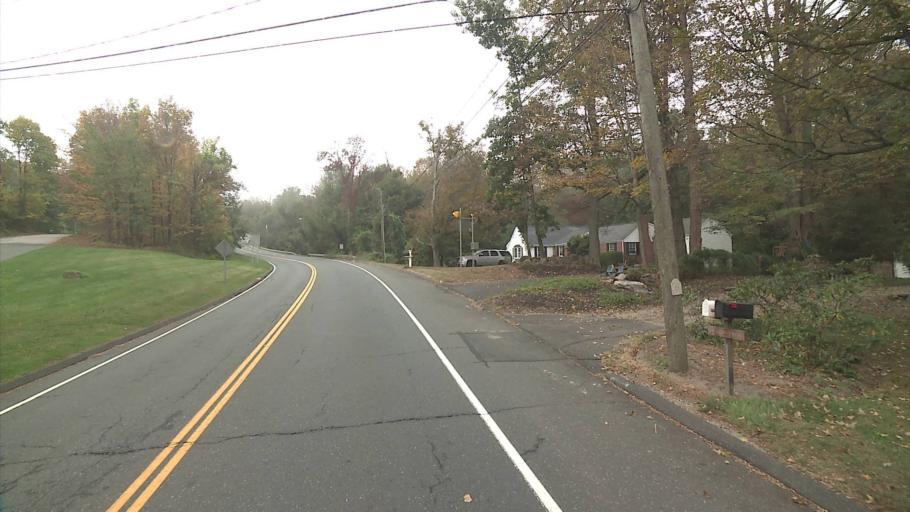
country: US
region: Connecticut
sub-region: Fairfield County
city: Newtown
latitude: 41.4172
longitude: -73.3160
